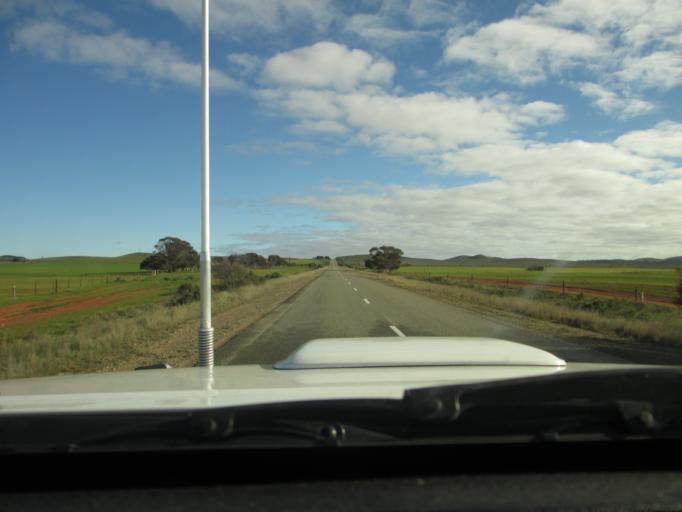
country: AU
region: South Australia
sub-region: Peterborough
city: Peterborough
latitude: -32.6302
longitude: 138.5902
